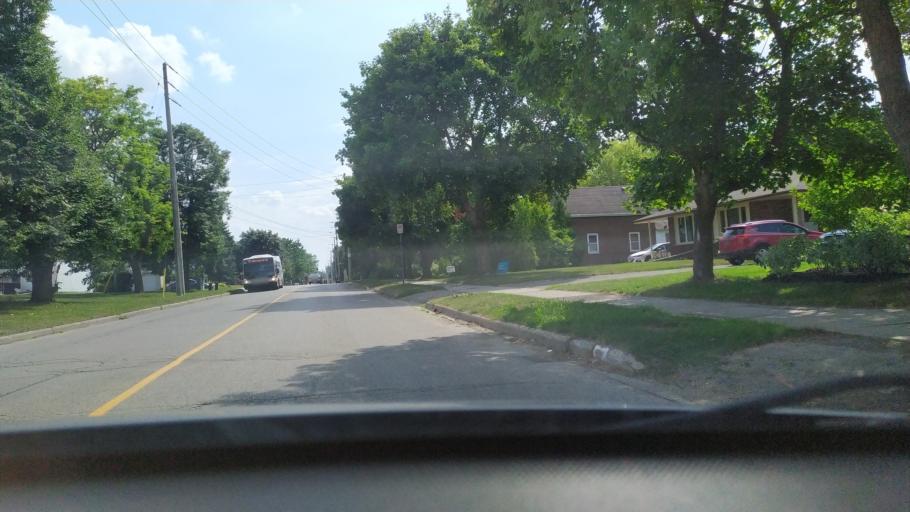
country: CA
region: Ontario
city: Stratford
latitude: 43.3824
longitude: -80.9947
